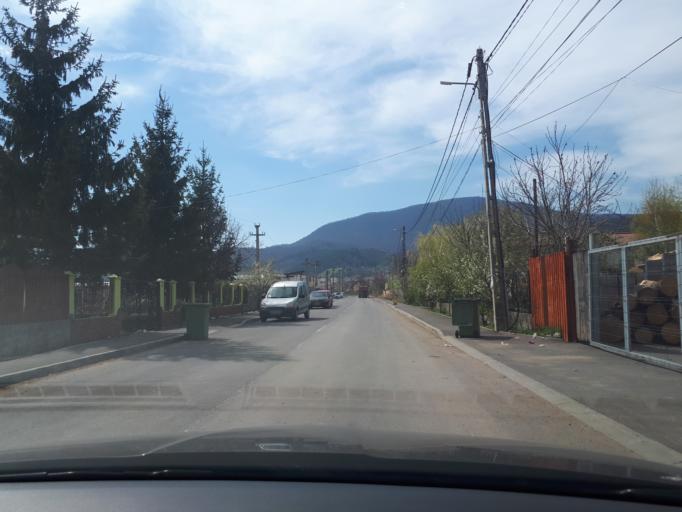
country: RO
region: Brasov
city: Codlea
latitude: 45.7043
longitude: 25.4610
